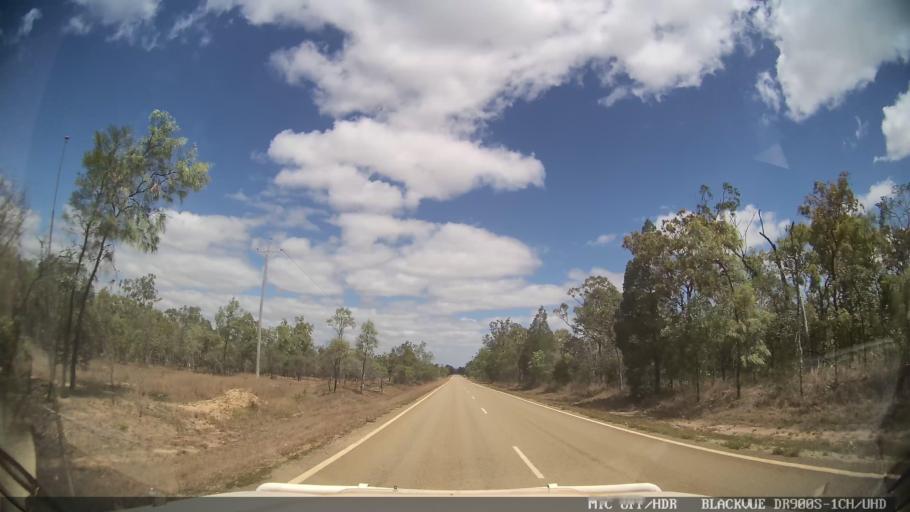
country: AU
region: Queensland
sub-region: Tablelands
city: Ravenshoe
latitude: -17.8117
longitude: 144.9577
